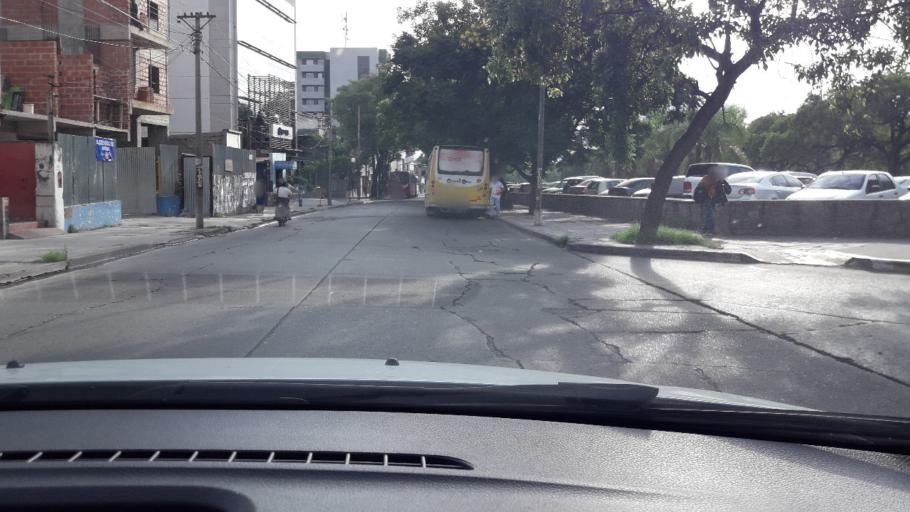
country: AR
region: Jujuy
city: San Salvador de Jujuy
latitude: -24.1888
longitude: -65.3012
